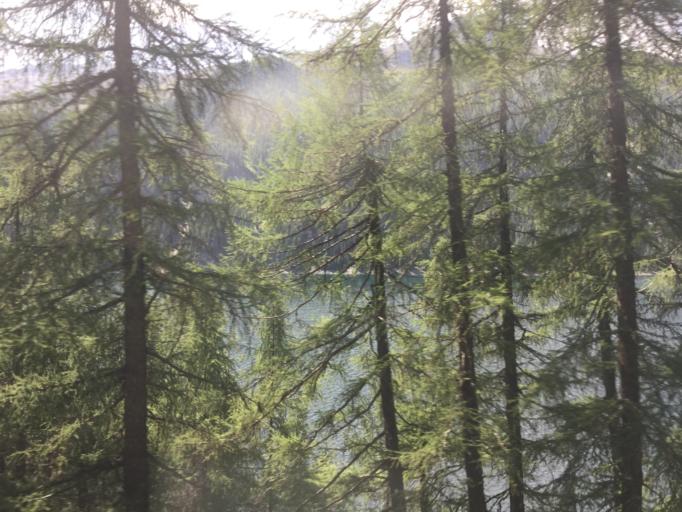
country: CH
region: Grisons
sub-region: Maloja District
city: Silvaplana
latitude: 46.5012
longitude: 9.6411
